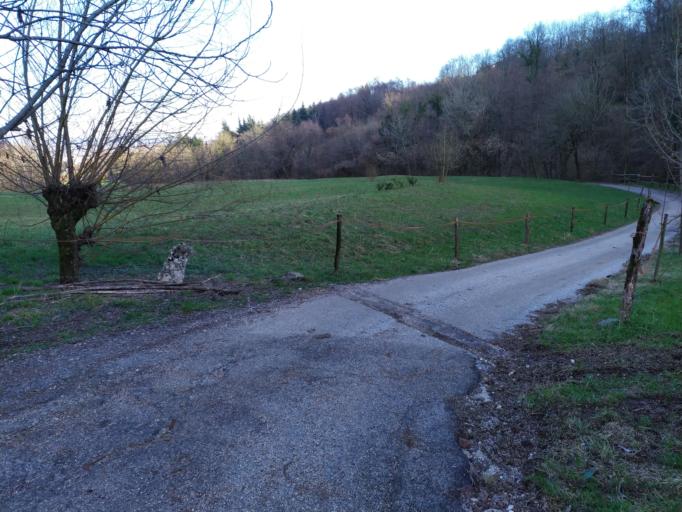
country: IT
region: Veneto
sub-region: Provincia di Vicenza
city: Monte di Malo
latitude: 45.6790
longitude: 11.3488
